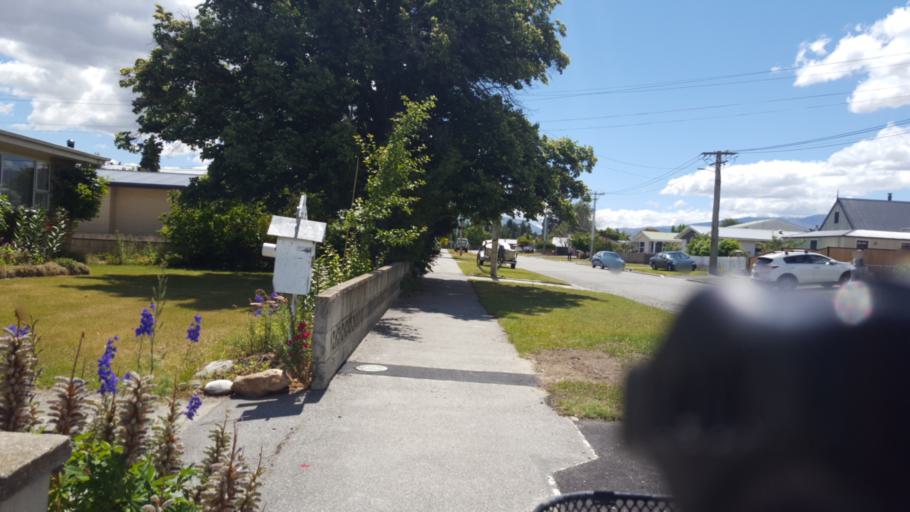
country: NZ
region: Otago
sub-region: Queenstown-Lakes District
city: Wanaka
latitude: -45.2428
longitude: 169.3902
